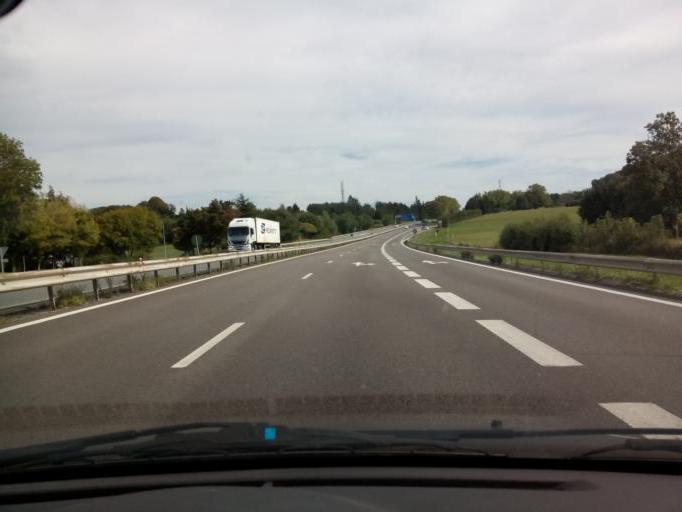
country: FR
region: Rhone-Alpes
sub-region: Departement de l'Isere
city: Saint-Victor-de-Cessieu
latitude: 45.5337
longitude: 5.4054
